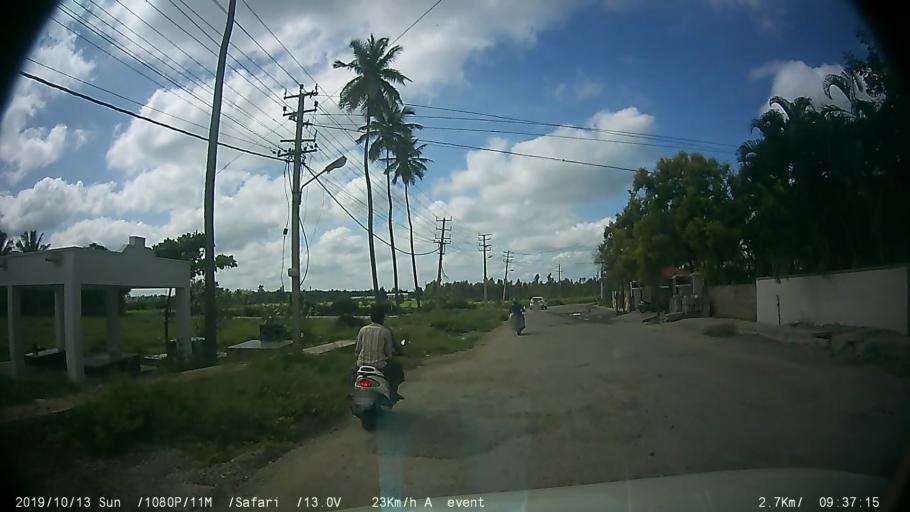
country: IN
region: Karnataka
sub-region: Bangalore Urban
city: Anekal
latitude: 12.8031
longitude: 77.6264
